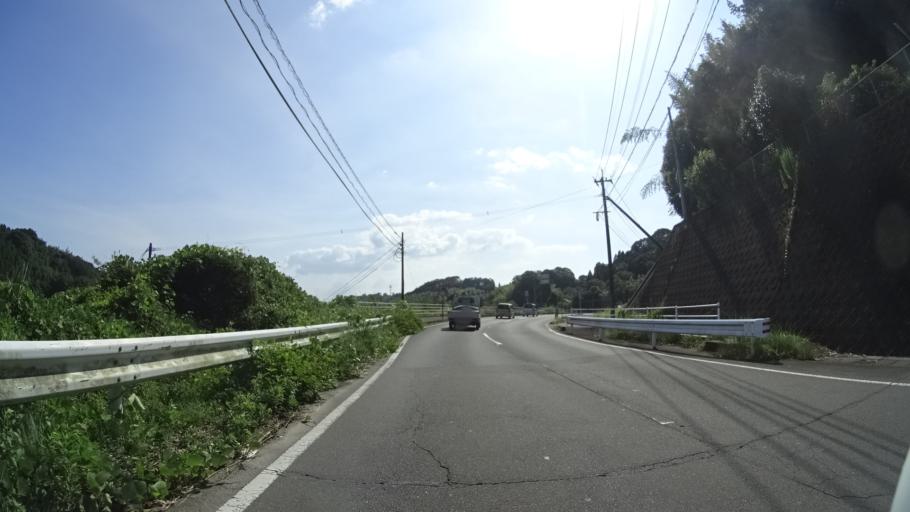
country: JP
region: Kagoshima
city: Kagoshima-shi
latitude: 31.6636
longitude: 130.5536
